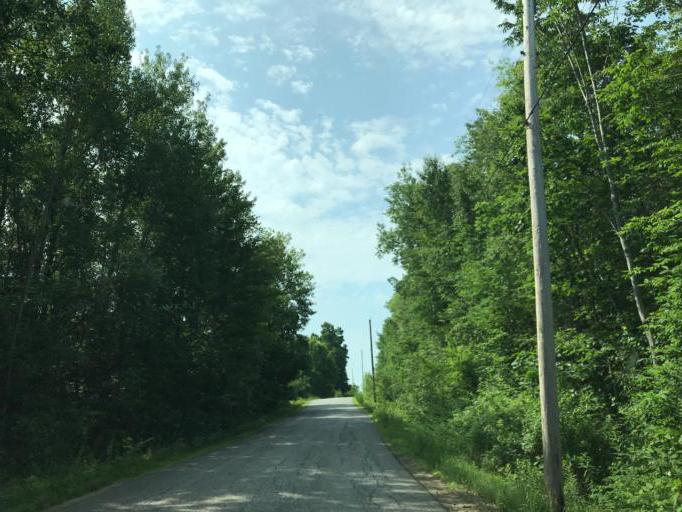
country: US
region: Maine
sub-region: Knox County
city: Hope
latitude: 44.2181
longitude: -69.1713
